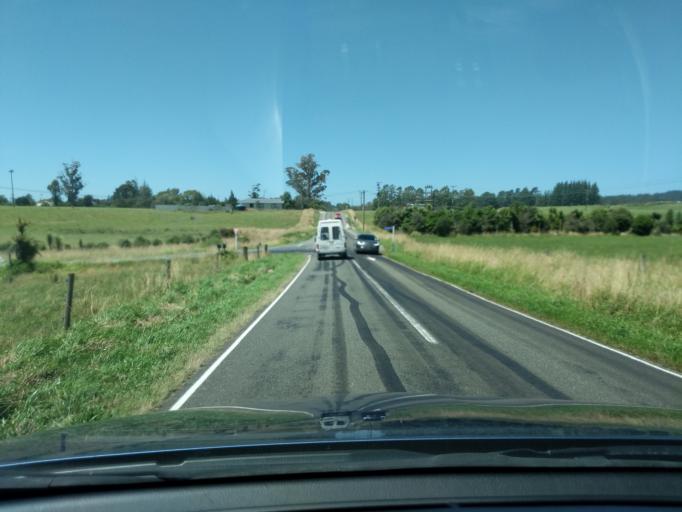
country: NZ
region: Tasman
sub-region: Tasman District
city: Takaka
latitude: -40.6871
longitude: 172.6497
